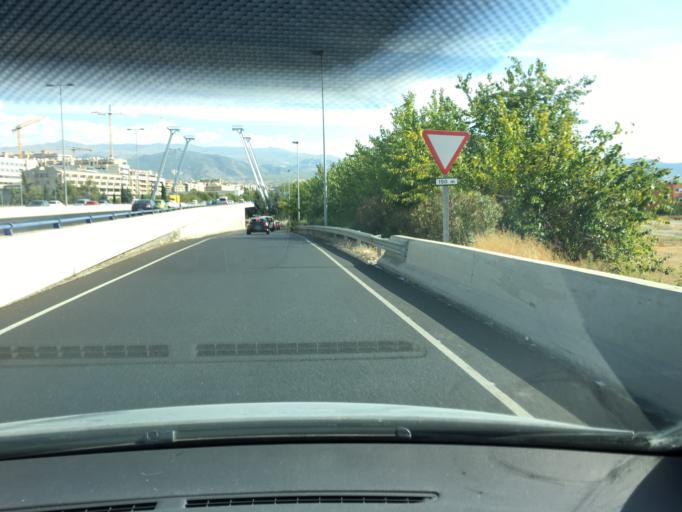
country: ES
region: Andalusia
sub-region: Provincia de Granada
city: Granada
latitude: 37.1778
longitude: -3.6159
